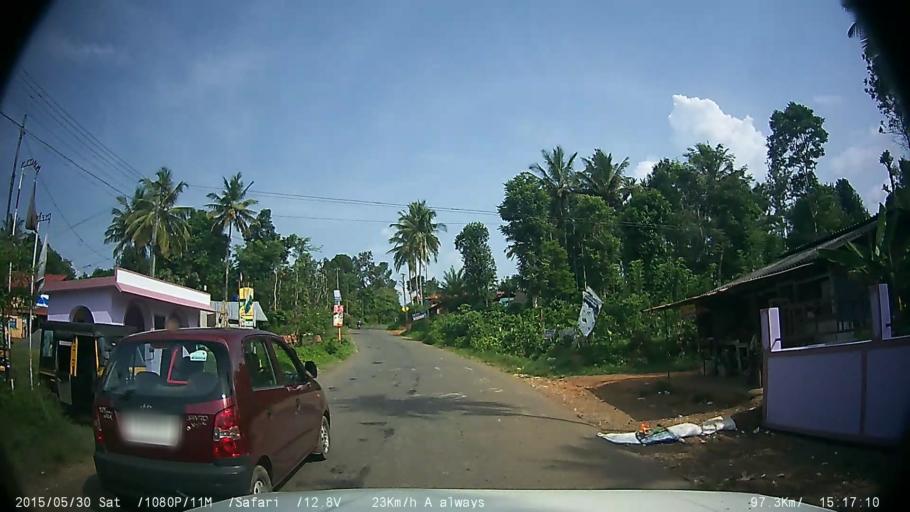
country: IN
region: Kerala
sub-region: Wayanad
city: Panamaram
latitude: 11.7739
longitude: 76.0594
